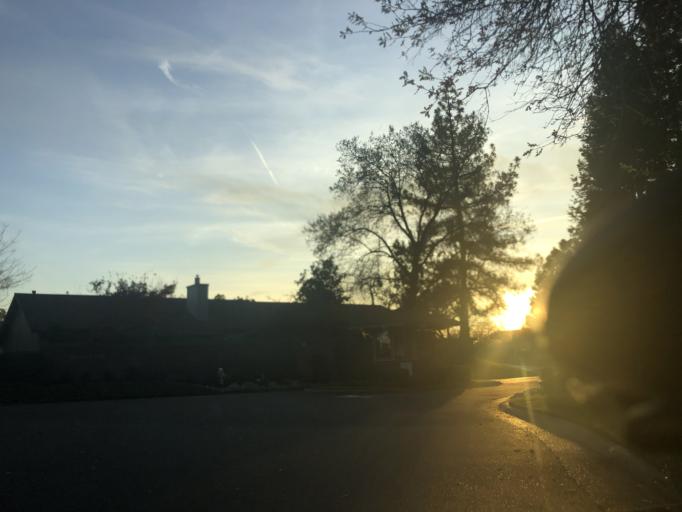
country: US
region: California
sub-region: Sacramento County
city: Gold River
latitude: 38.6374
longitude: -121.2271
